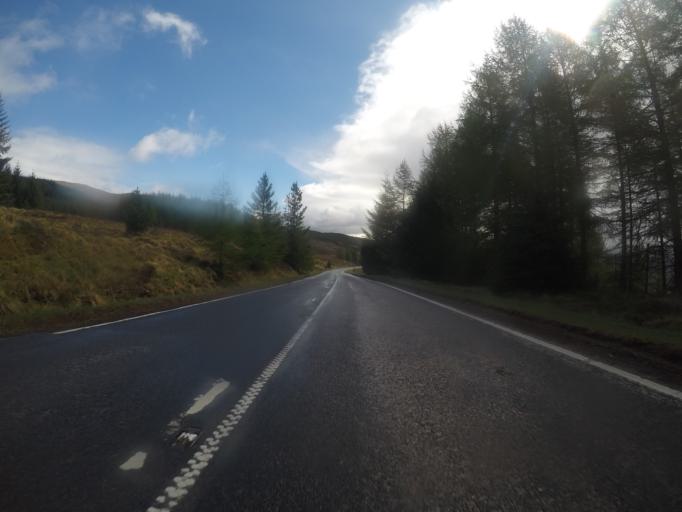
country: GB
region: Scotland
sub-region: Highland
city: Spean Bridge
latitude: 57.0875
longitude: -4.9765
